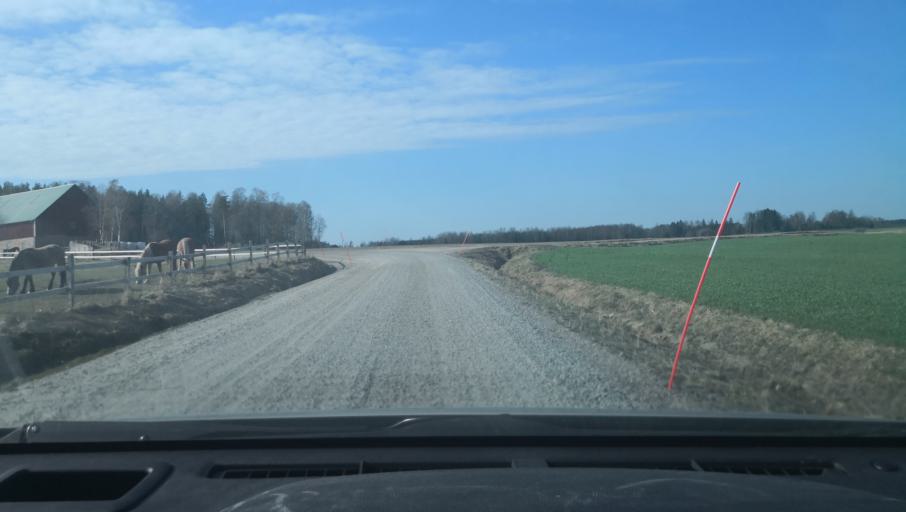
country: SE
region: Uppsala
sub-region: Heby Kommun
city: Morgongava
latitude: 59.8450
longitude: 16.9135
